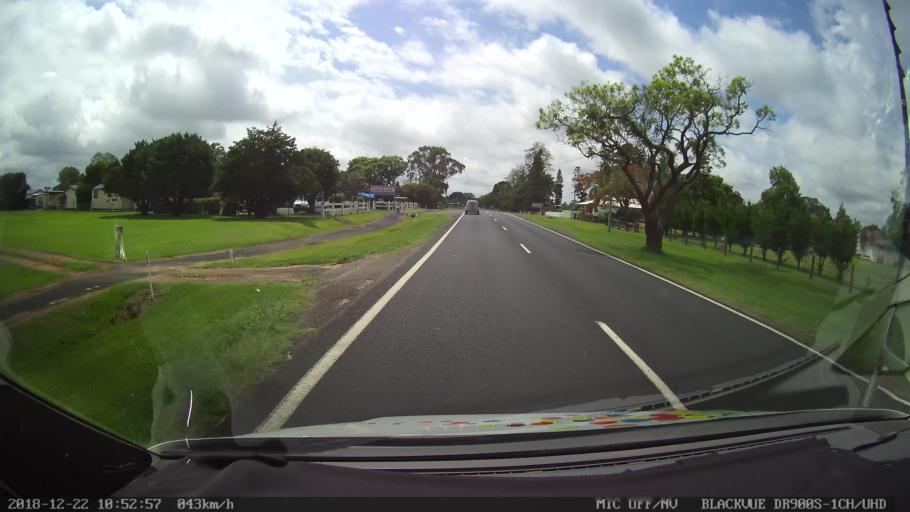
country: AU
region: New South Wales
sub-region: Clarence Valley
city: South Grafton
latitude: -29.6952
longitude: 152.9136
